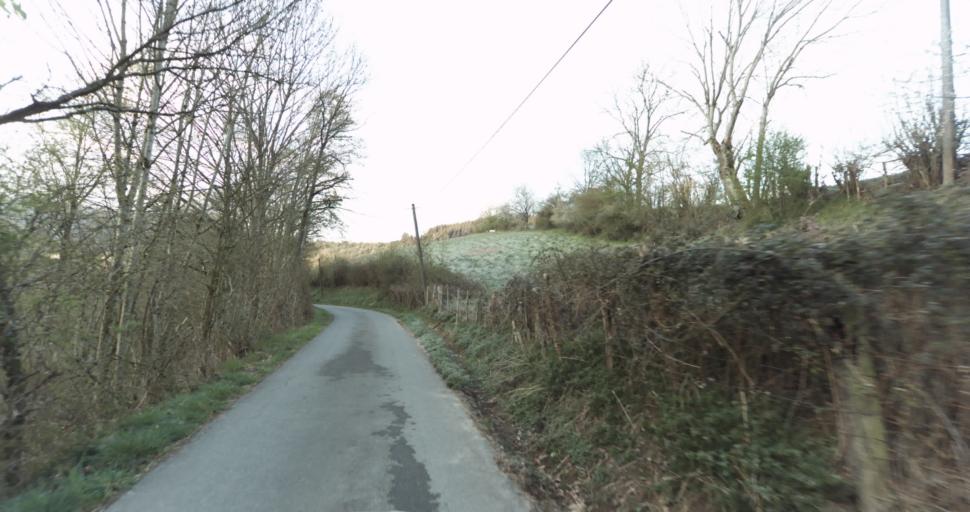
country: FR
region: Rhone-Alpes
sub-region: Departement du Rhone
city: Tarare
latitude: 45.8972
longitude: 4.3997
